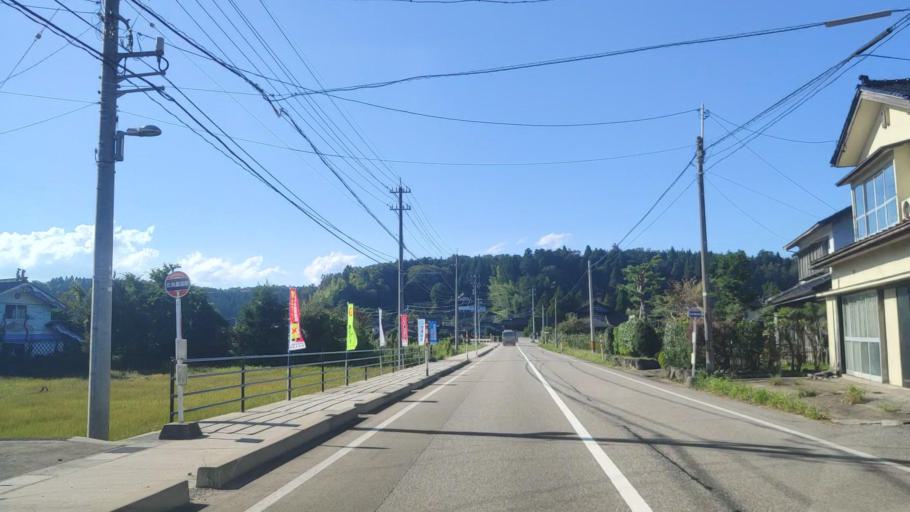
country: JP
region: Ishikawa
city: Nanao
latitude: 37.2356
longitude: 136.9648
